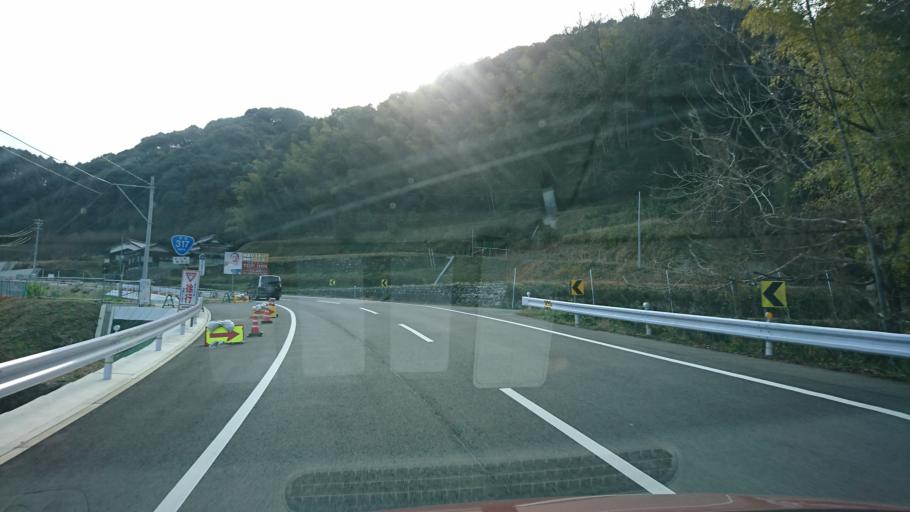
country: JP
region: Ehime
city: Hojo
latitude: 33.9870
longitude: 132.9083
